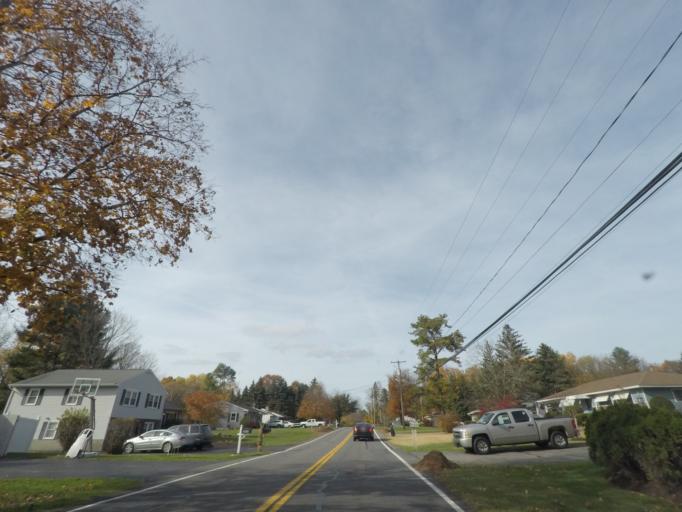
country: US
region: New York
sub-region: Schenectady County
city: Rotterdam
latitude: 42.7521
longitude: -73.9392
